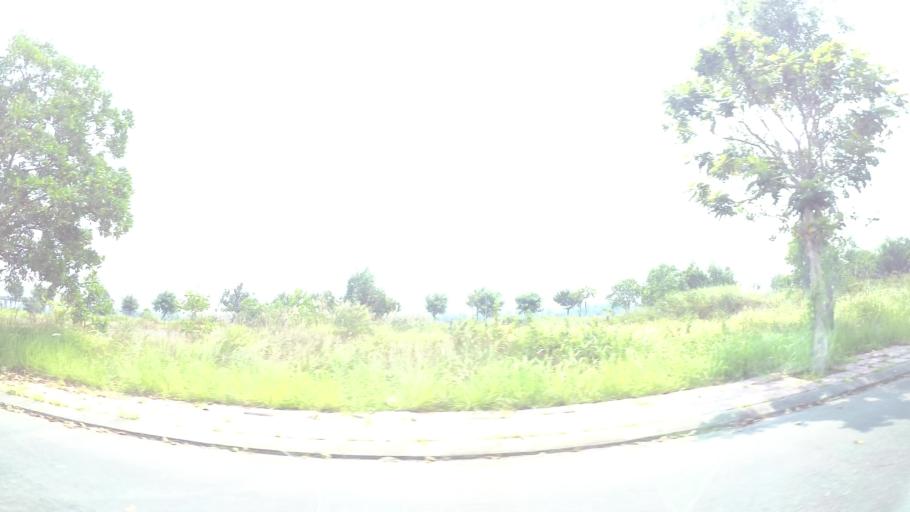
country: VN
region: Da Nang
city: Cam Le
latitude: 16.0137
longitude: 108.2103
